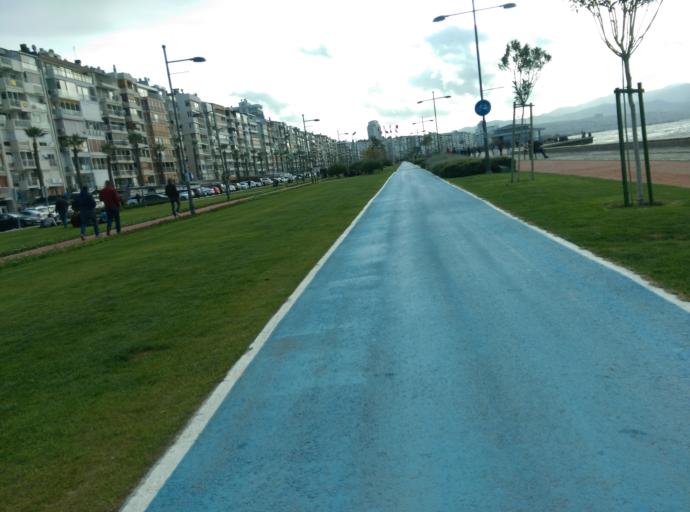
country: TR
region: Izmir
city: Izmir
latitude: 38.4407
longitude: 27.1421
